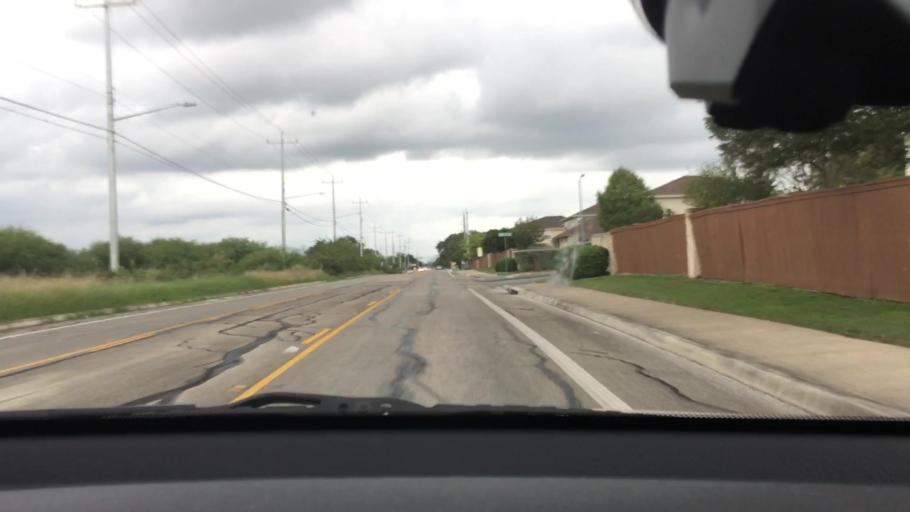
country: US
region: Texas
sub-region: Bexar County
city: Converse
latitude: 29.5323
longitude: -98.3123
